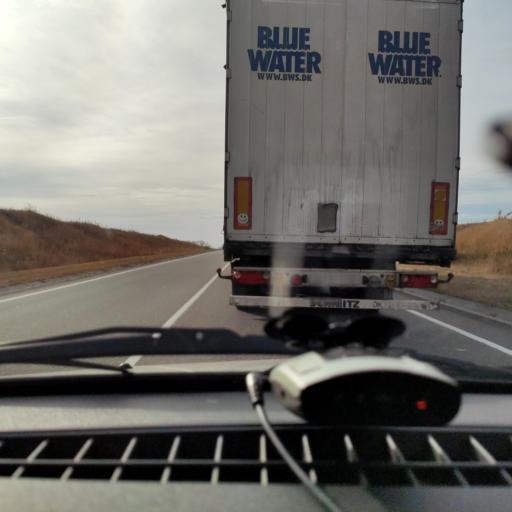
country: RU
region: Voronezj
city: Strelitsa
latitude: 51.5186
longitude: 38.9681
